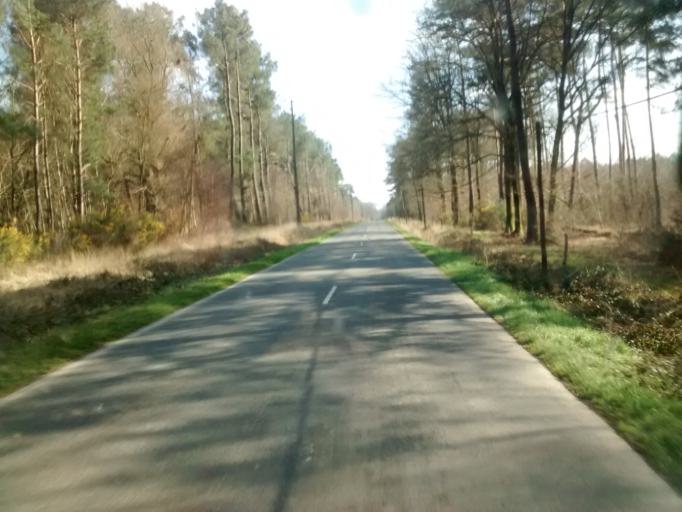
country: FR
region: Brittany
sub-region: Departement d'Ille-et-Vilaine
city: Paimpont
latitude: 48.0316
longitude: -2.1770
